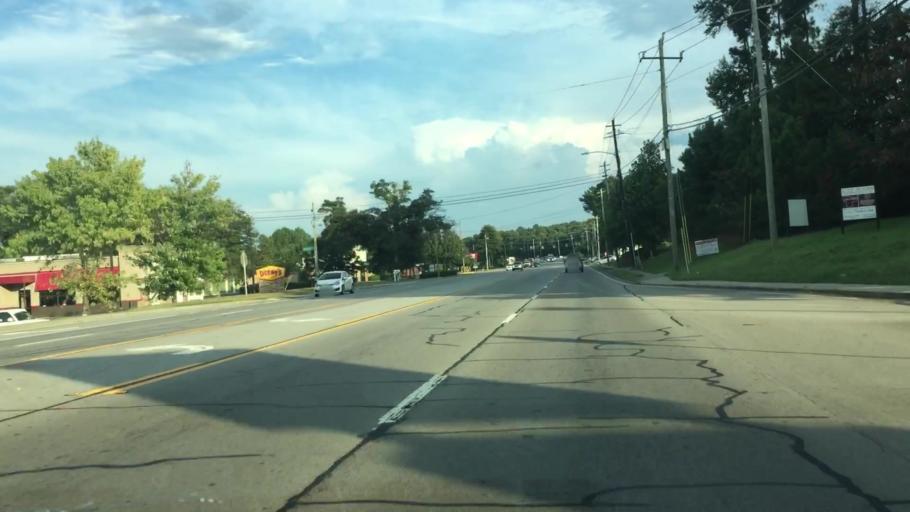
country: US
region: Georgia
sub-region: Henry County
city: Stockbridge
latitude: 33.5493
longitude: -84.2541
